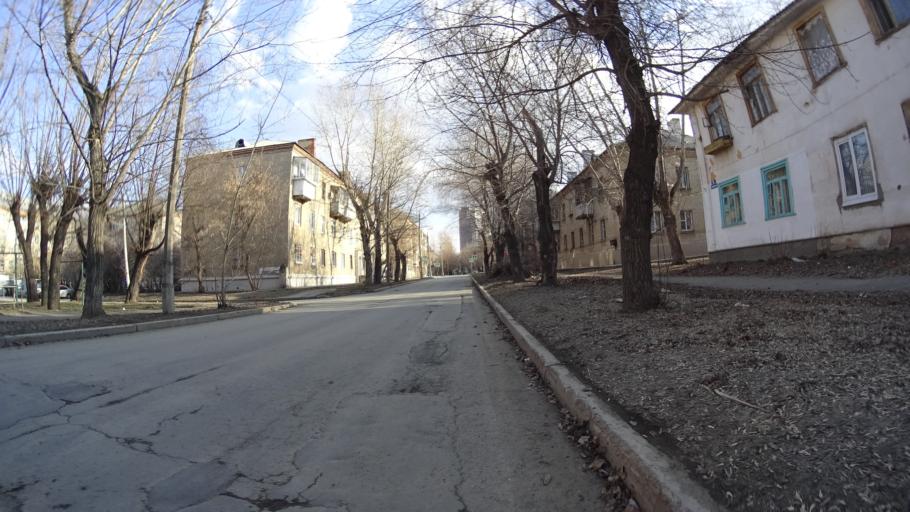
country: RU
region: Chelyabinsk
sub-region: Gorod Chelyabinsk
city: Chelyabinsk
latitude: 55.1465
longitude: 61.3747
